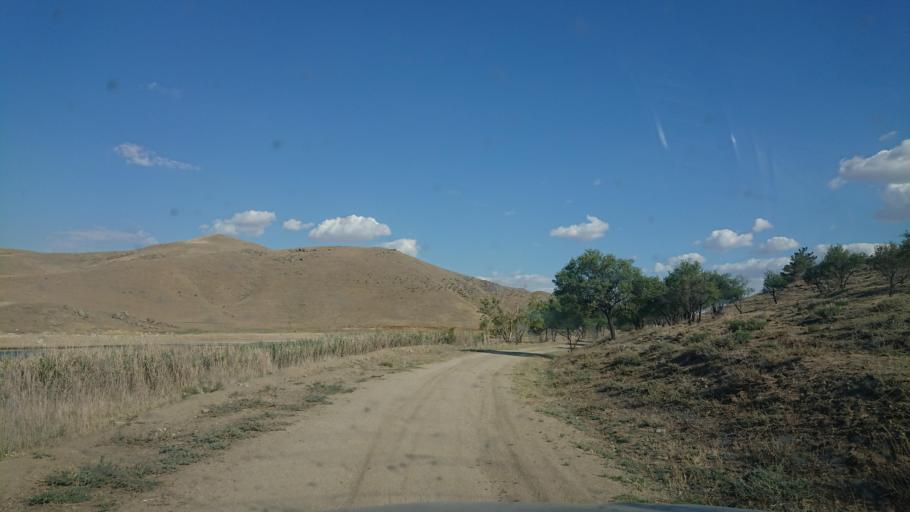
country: TR
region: Aksaray
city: Sariyahsi
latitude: 39.0219
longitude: 33.8959
